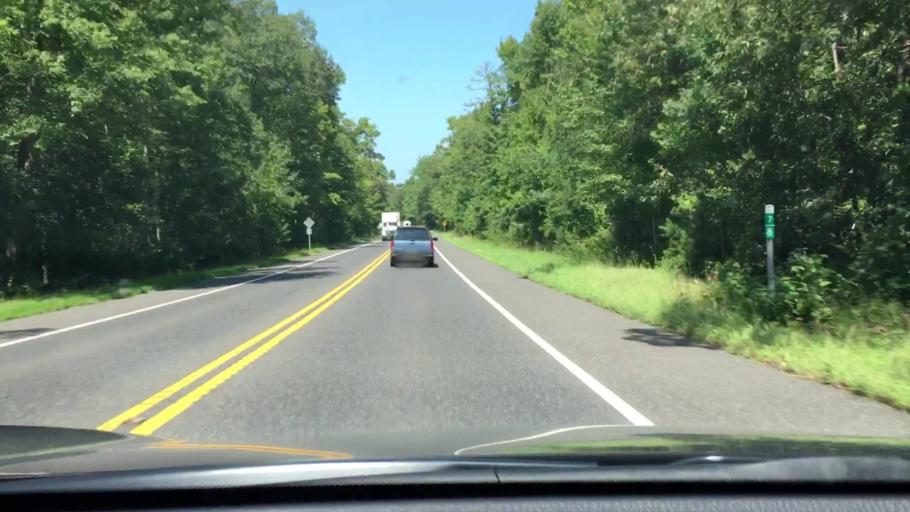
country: US
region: New Jersey
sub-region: Cumberland County
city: Port Norris
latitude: 39.2868
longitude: -74.9584
